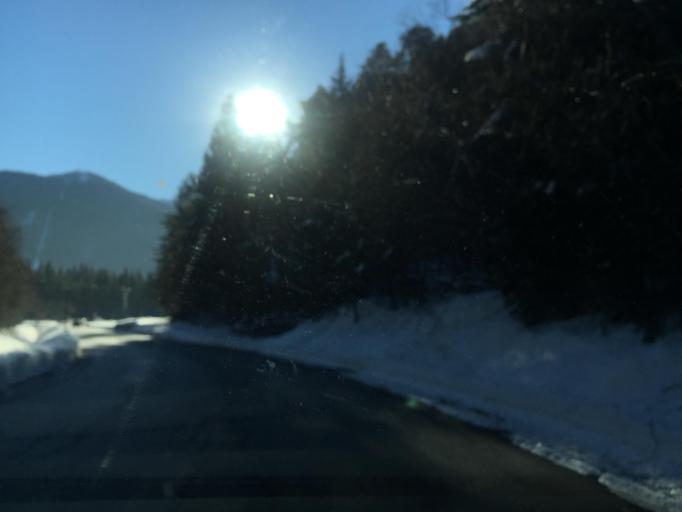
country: IT
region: Friuli Venezia Giulia
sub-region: Provincia di Udine
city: Malborghetto
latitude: 46.5065
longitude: 13.4825
